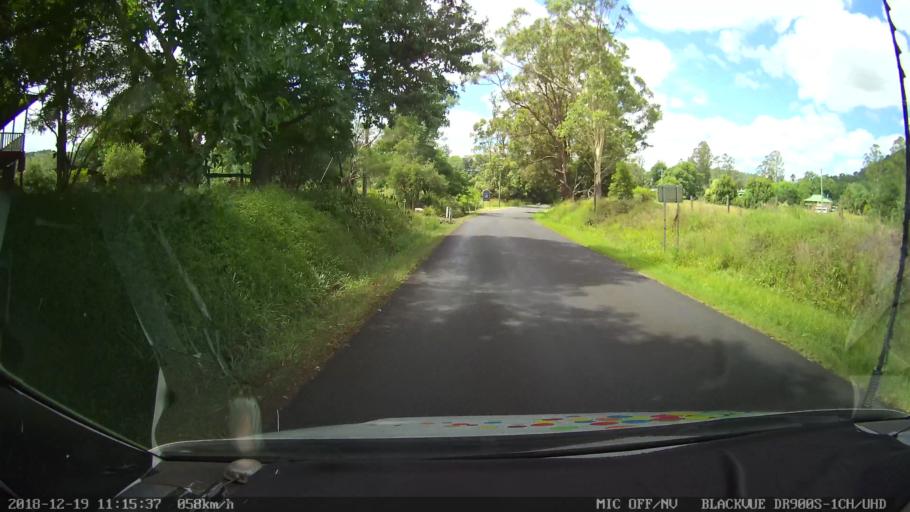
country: AU
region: New South Wales
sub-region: Lismore Municipality
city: Nimbin
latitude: -28.6695
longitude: 153.2785
